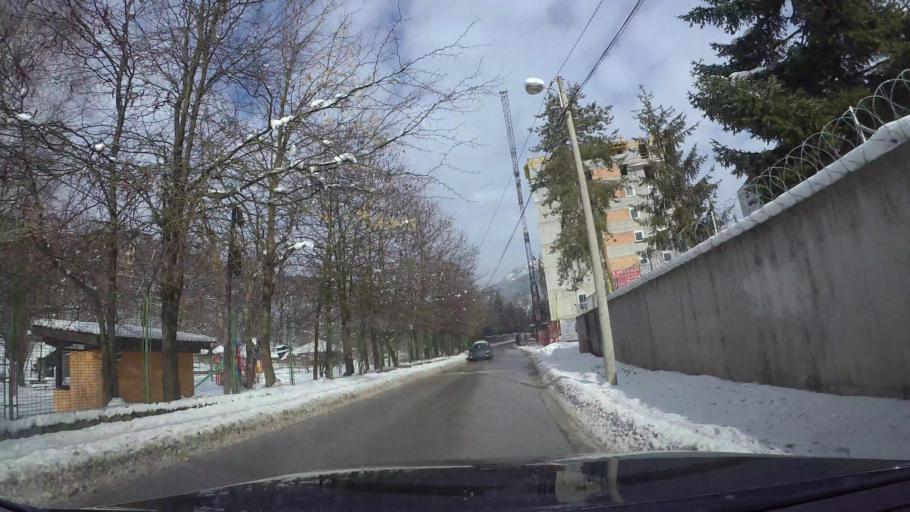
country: BA
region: Federation of Bosnia and Herzegovina
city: Kobilja Glava
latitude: 43.8801
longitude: 18.4138
